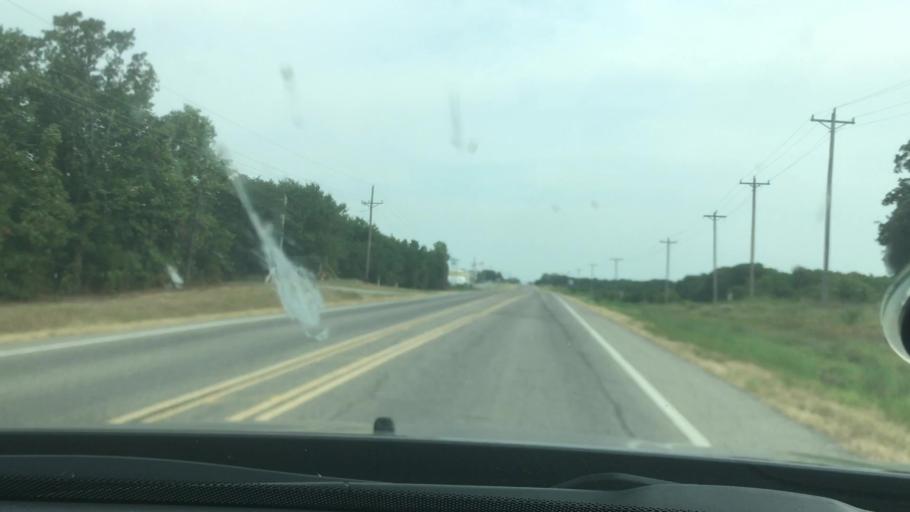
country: US
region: Oklahoma
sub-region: Bryan County
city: Durant
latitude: 34.2271
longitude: -96.4248
